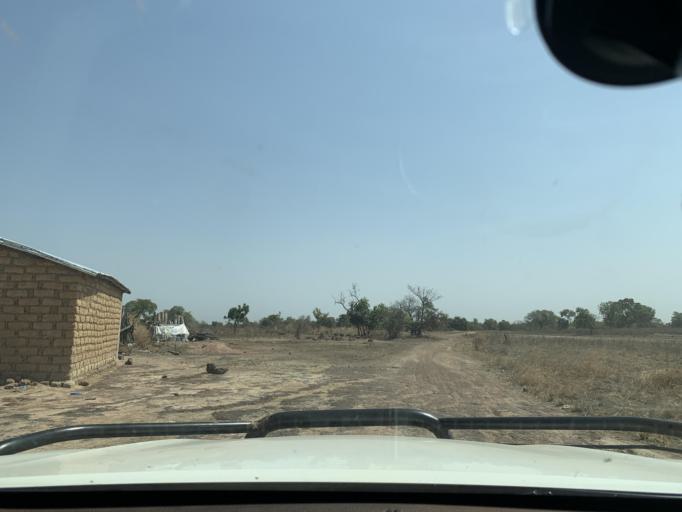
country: ML
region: Sikasso
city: Kolondieba
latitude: 10.8416
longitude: -6.8032
